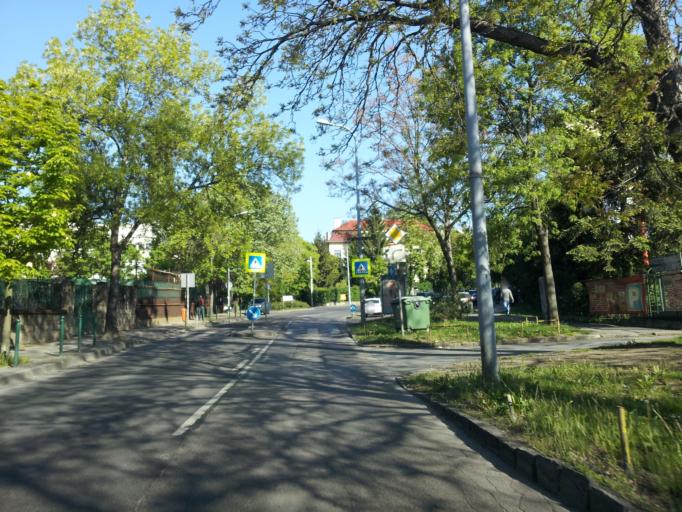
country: HU
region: Budapest
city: Budapest XII. keruelet
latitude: 47.5120
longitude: 19.0081
